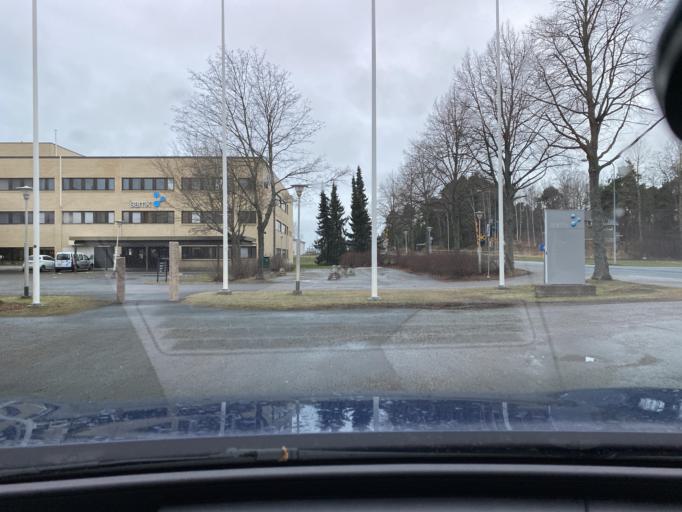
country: FI
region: Satakunta
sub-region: Rauma
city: Rauma
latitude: 61.1280
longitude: 21.4827
